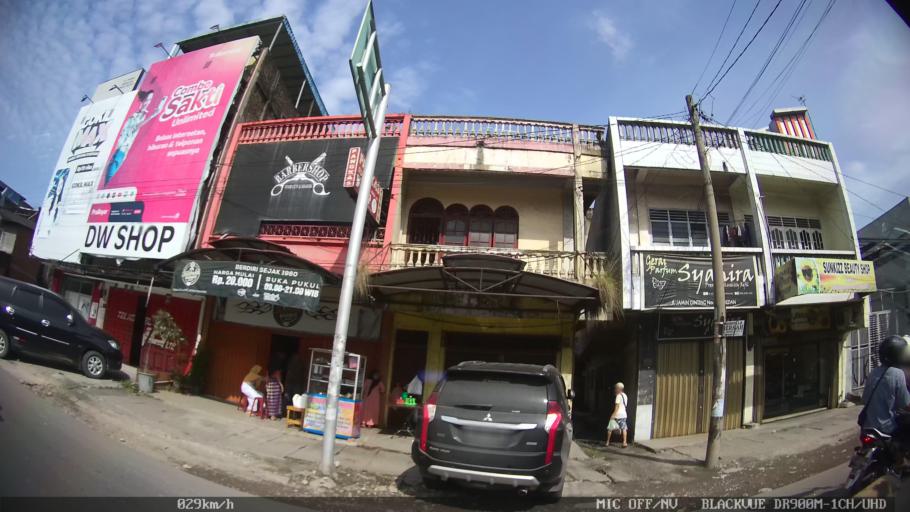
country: ID
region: North Sumatra
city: Medan
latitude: 3.5710
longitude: 98.6599
